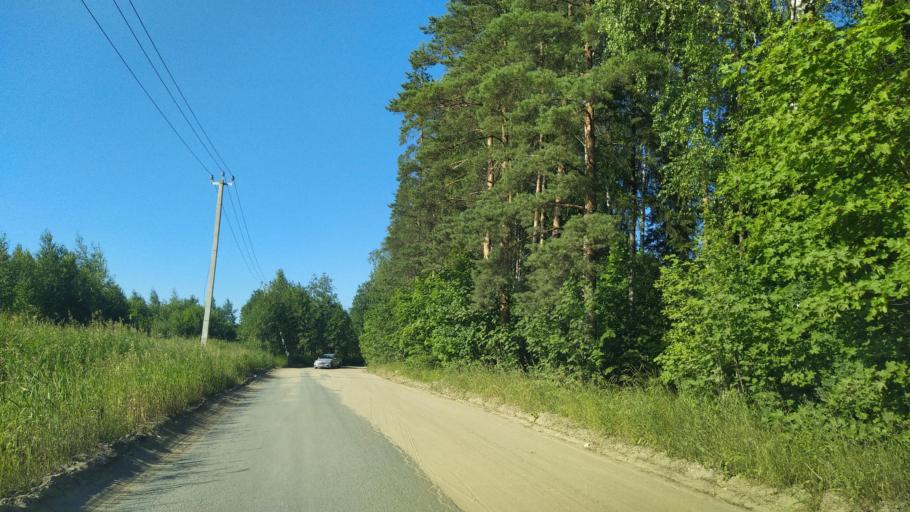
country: RU
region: Leningrad
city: Koltushi
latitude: 59.9046
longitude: 30.7346
